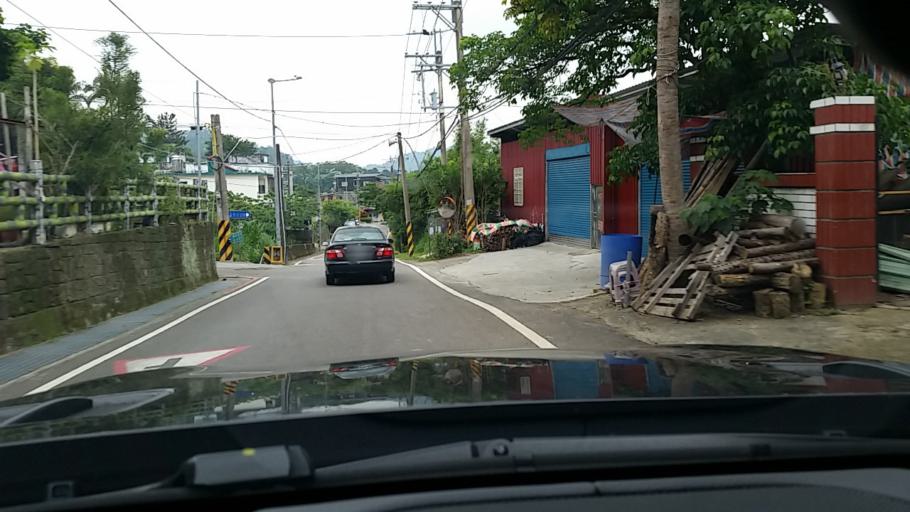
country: TW
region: Taiwan
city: Daxi
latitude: 24.8005
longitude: 121.3068
